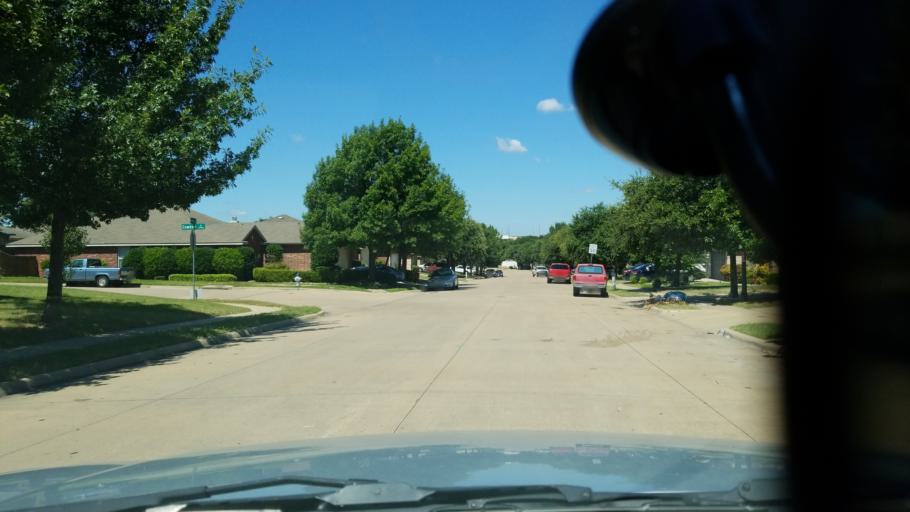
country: US
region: Texas
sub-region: Dallas County
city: Duncanville
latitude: 32.6604
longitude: -96.8645
